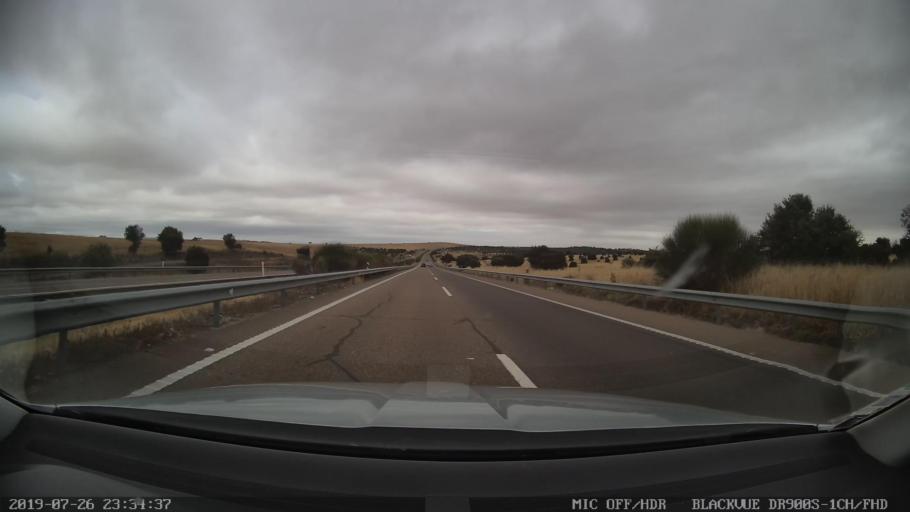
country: ES
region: Extremadura
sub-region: Provincia de Caceres
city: Santa Cruz de la Sierra
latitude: 39.3625
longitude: -5.8689
